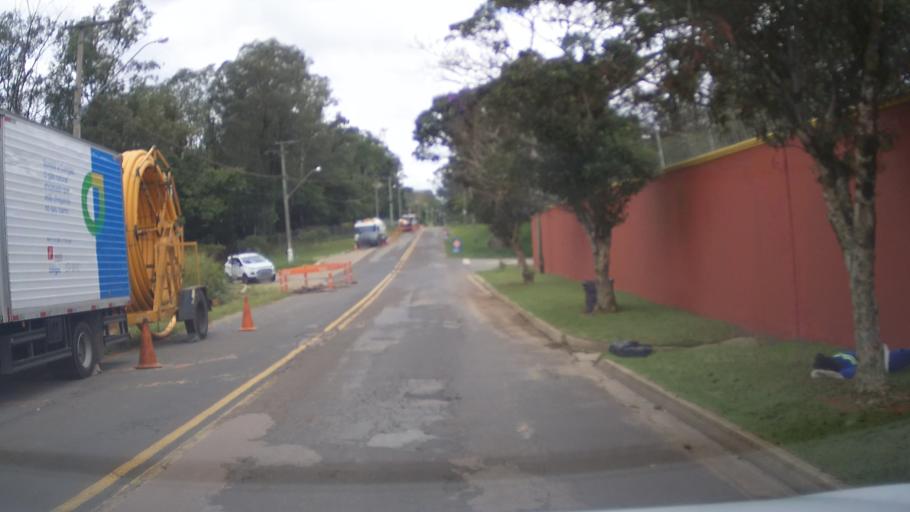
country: BR
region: Sao Paulo
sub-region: Vinhedo
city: Vinhedo
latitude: -23.0183
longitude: -46.9596
